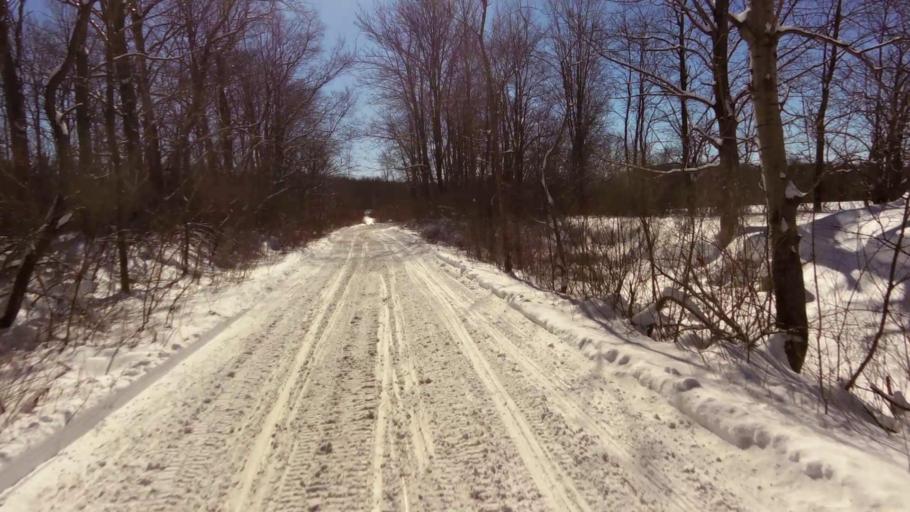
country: US
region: New York
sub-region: Chautauqua County
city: Mayville
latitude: 42.1576
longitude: -79.5864
